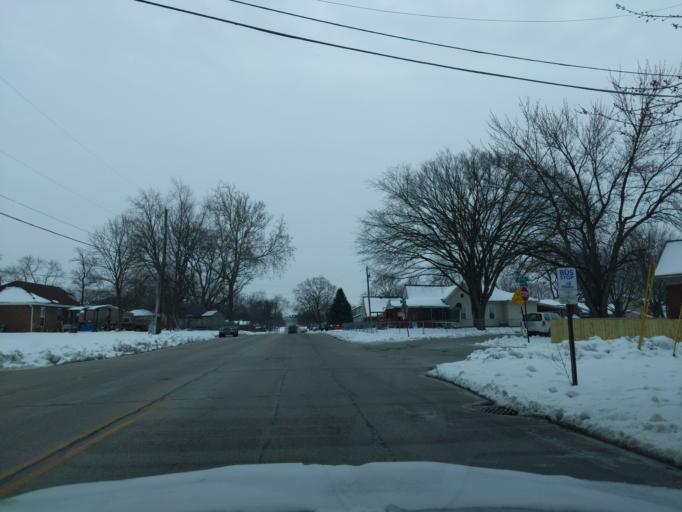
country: US
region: Indiana
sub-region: Tippecanoe County
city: Lafayette
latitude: 40.4048
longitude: -86.8746
